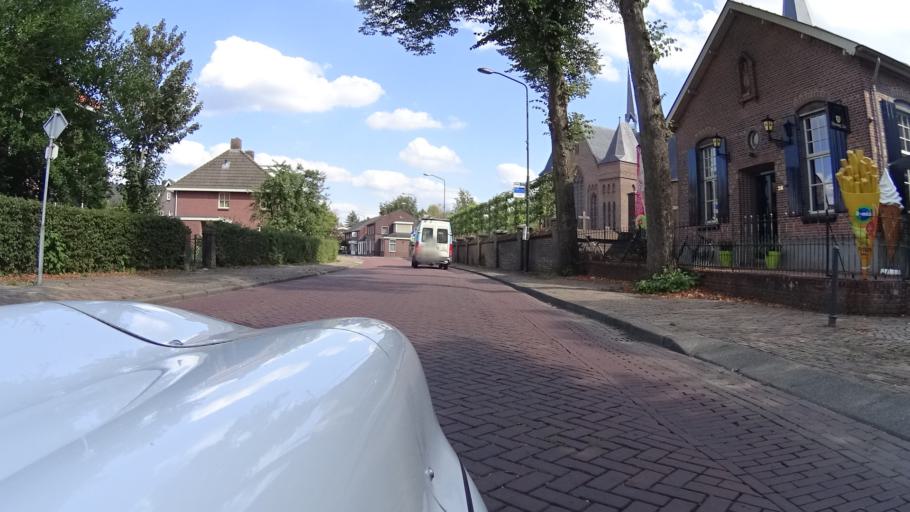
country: NL
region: North Brabant
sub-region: Gemeente Sint Anthonis
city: Sint Anthonis
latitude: 51.6271
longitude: 5.8818
